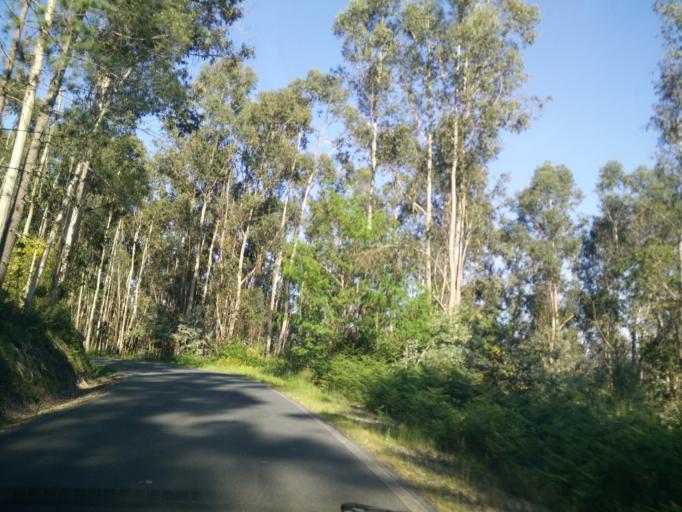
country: ES
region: Galicia
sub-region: Provincia de Pontevedra
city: Mondariz
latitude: 42.2521
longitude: -8.4199
